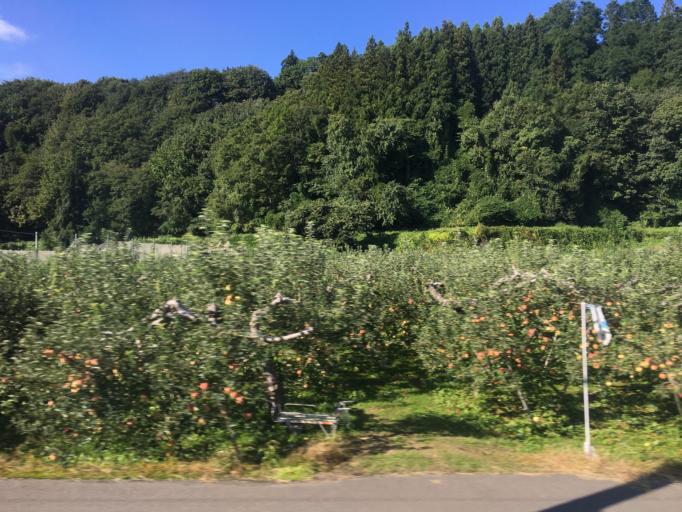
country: JP
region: Aomori
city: Hirosaki
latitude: 40.5367
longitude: 140.5466
